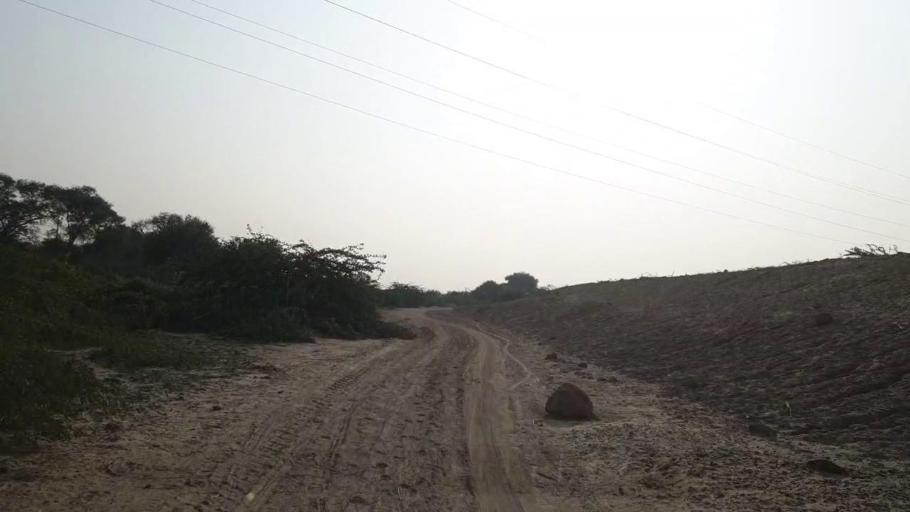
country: PK
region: Sindh
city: Tando Muhammad Khan
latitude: 25.1066
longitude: 68.3022
